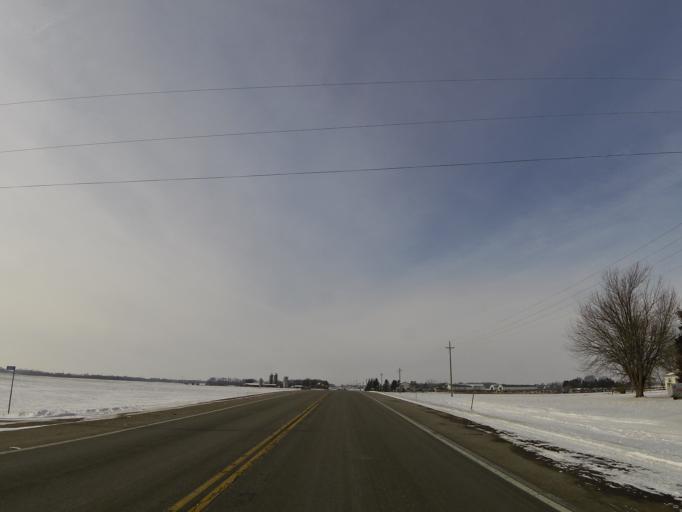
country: US
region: Minnesota
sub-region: McLeod County
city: Lester Prairie
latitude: 44.9063
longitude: -94.0234
